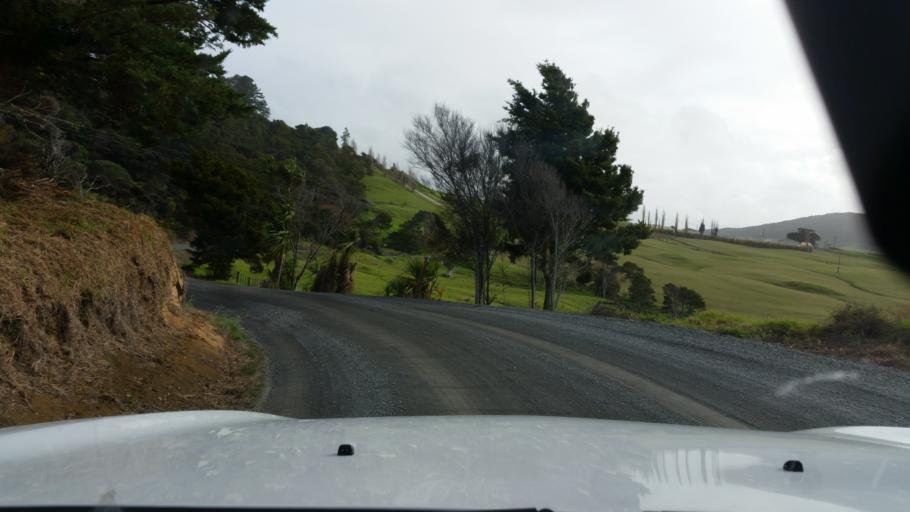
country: NZ
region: Northland
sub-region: Whangarei
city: Ruakaka
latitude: -35.7971
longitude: 174.5307
